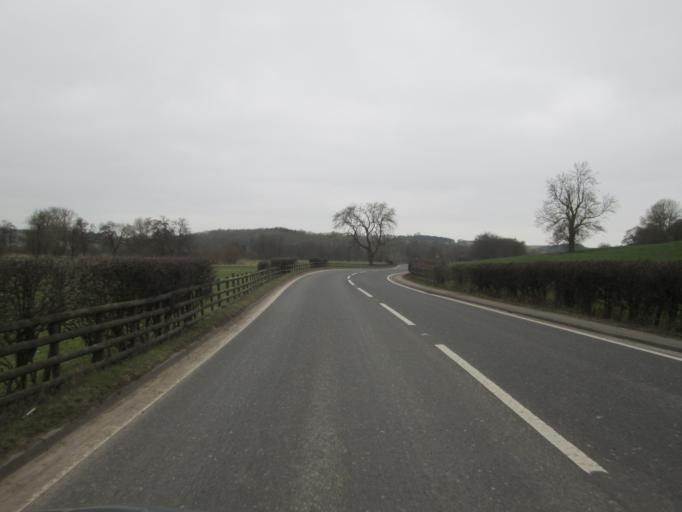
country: GB
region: England
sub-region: Derbyshire
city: Bakewell
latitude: 53.1899
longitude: -1.6320
